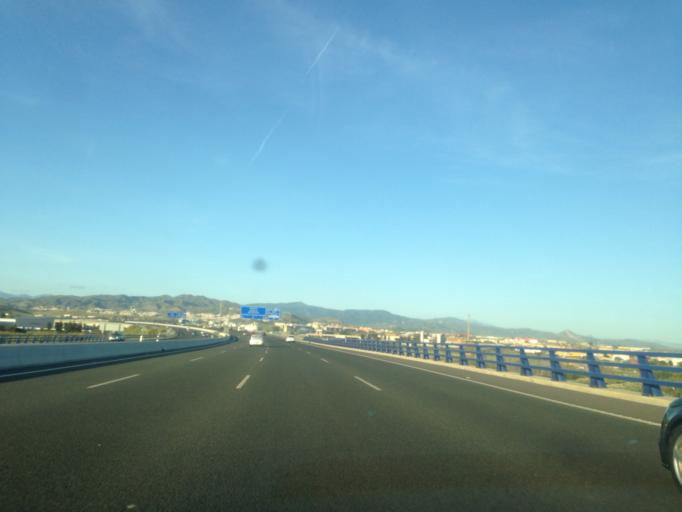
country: ES
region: Andalusia
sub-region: Provincia de Malaga
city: Alhaurin de la Torre
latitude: 36.6974
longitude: -4.5193
